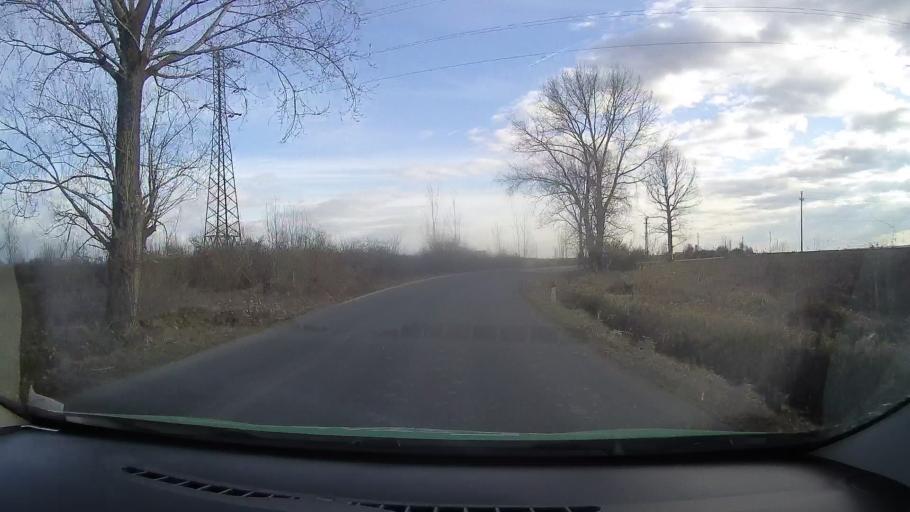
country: RO
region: Dambovita
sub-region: Comuna Ulmi
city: Ulmi
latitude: 44.8883
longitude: 25.4646
